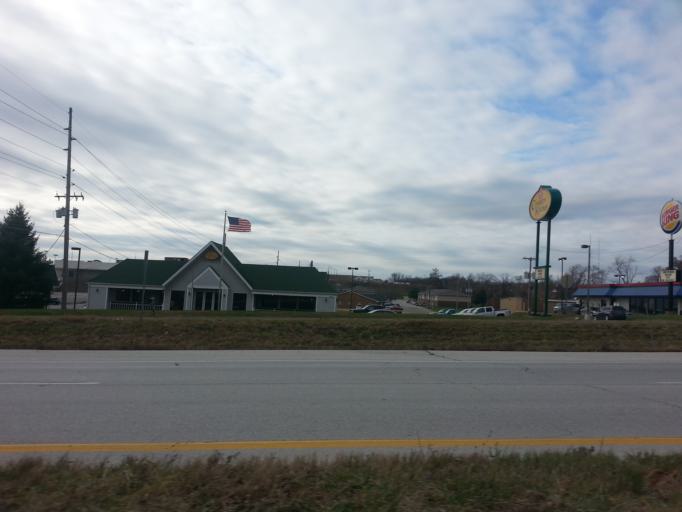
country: US
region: Missouri
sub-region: Marion County
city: Hannibal
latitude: 39.7255
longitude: -91.3919
